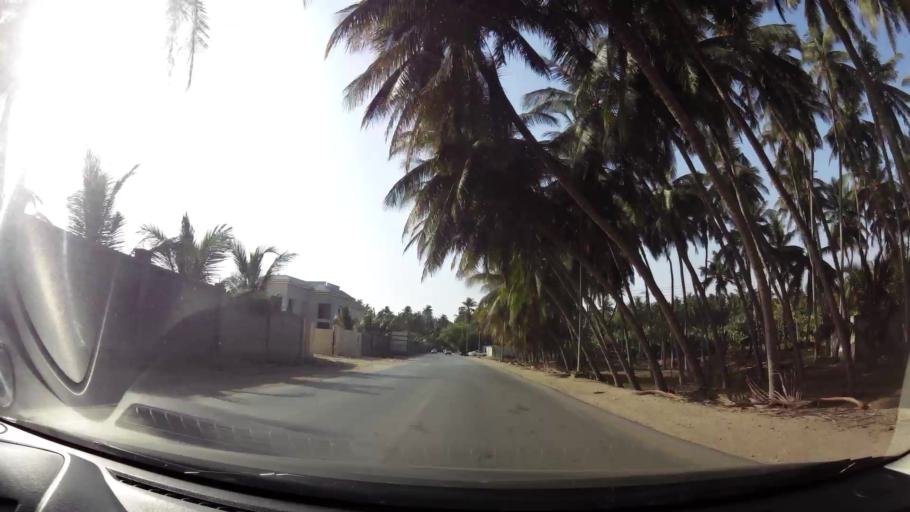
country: OM
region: Zufar
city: Salalah
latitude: 17.0054
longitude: 54.0986
